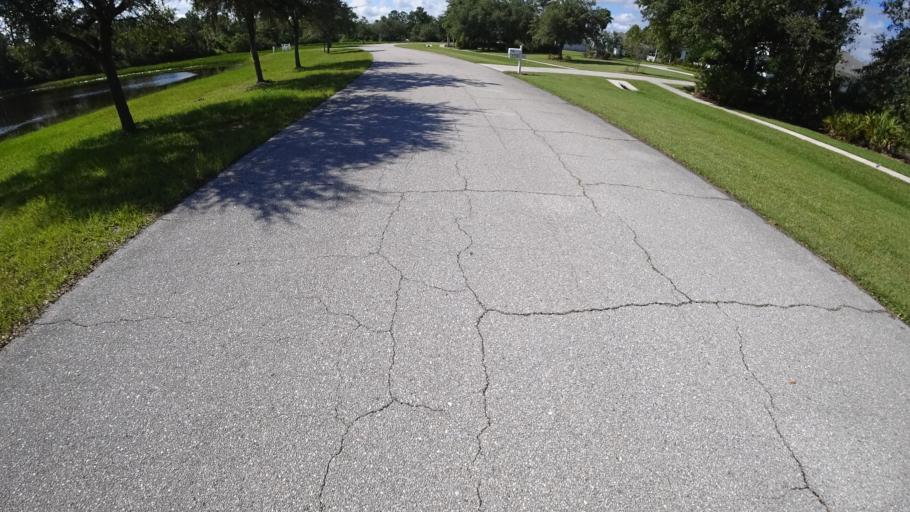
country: US
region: Florida
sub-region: Sarasota County
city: The Meadows
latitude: 27.4032
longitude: -82.3199
